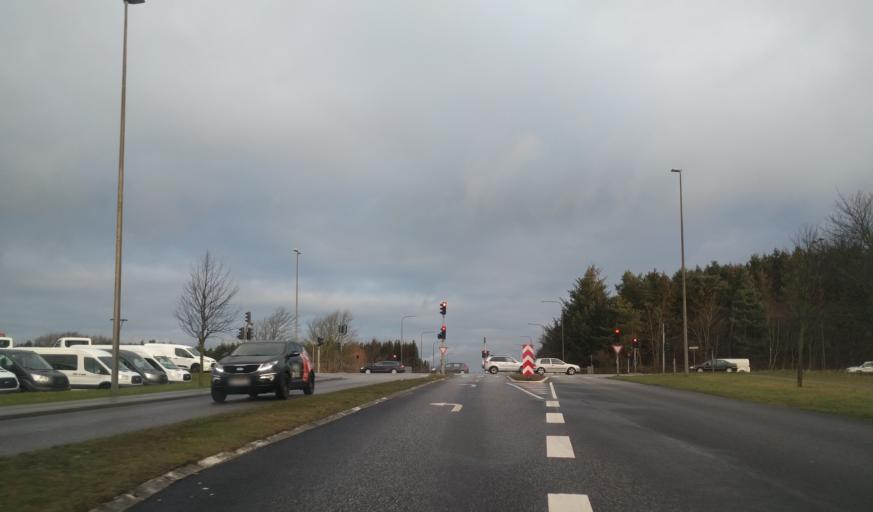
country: DK
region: North Denmark
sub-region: Alborg Kommune
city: Gistrup
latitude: 57.0299
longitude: 9.9768
